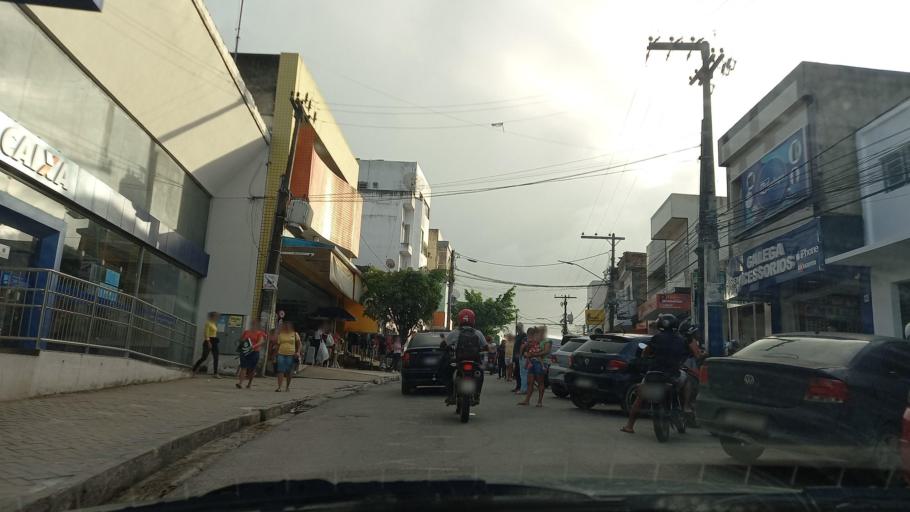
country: BR
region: Pernambuco
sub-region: Palmares
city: Palmares
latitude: -8.6859
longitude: -35.5918
